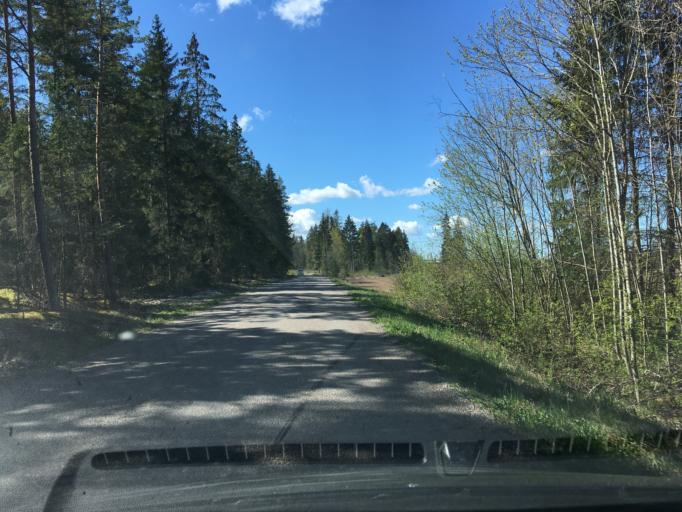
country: EE
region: Harju
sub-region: Rae vald
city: Vaida
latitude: 59.1989
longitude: 25.0743
